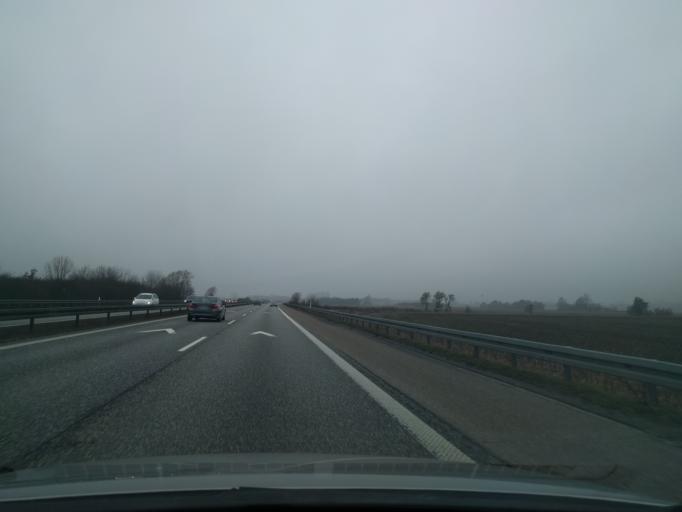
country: DK
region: Zealand
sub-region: Soro Kommune
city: Frederiksberg
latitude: 55.4510
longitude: 11.6617
